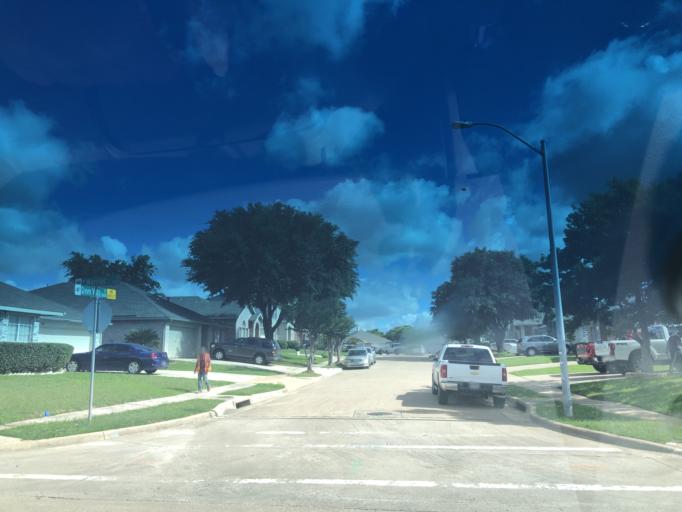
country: US
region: Texas
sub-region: Dallas County
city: Grand Prairie
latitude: 32.6986
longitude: -97.0290
